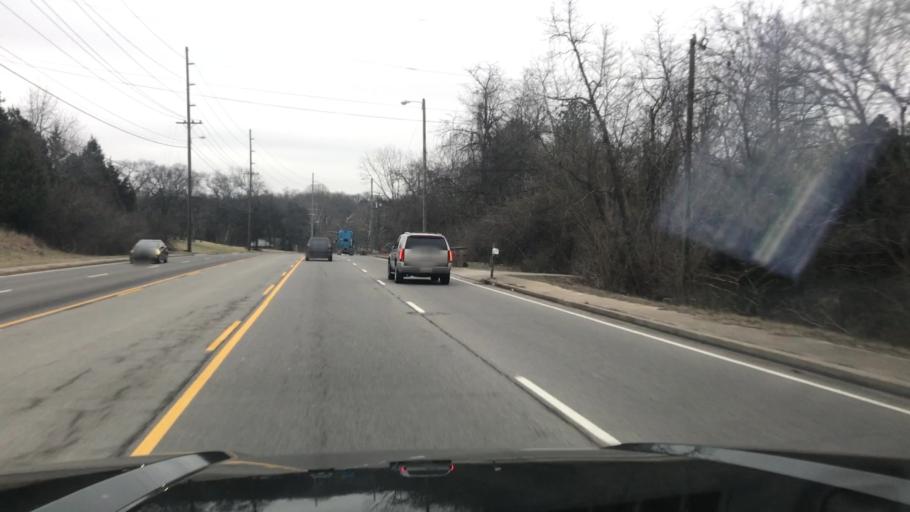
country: US
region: Tennessee
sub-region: Williamson County
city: Brentwood Estates
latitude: 36.0451
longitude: -86.6979
